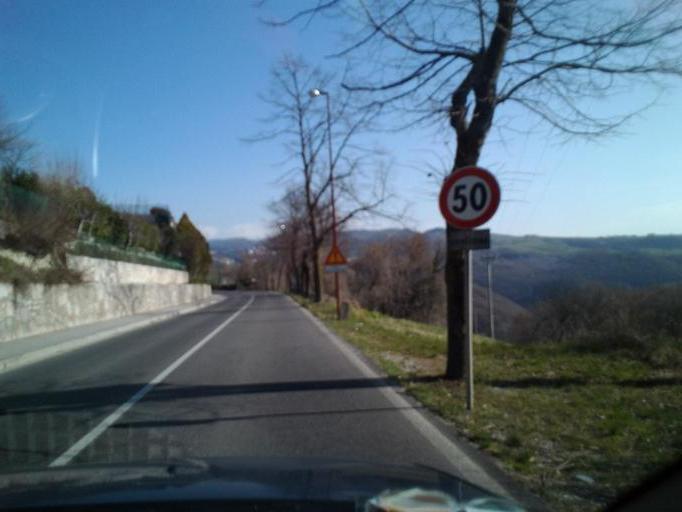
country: IT
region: Veneto
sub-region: Provincia di Verona
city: Cerro Veronese
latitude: 45.5689
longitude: 11.0432
